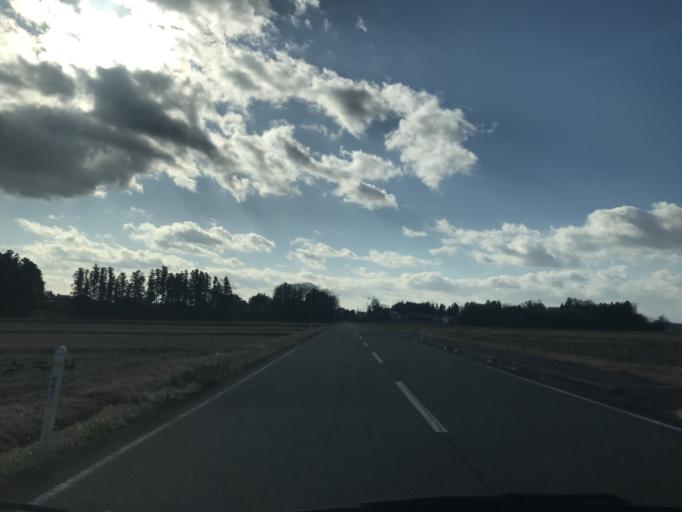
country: JP
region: Iwate
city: Ichinoseki
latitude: 38.7648
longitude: 141.0595
